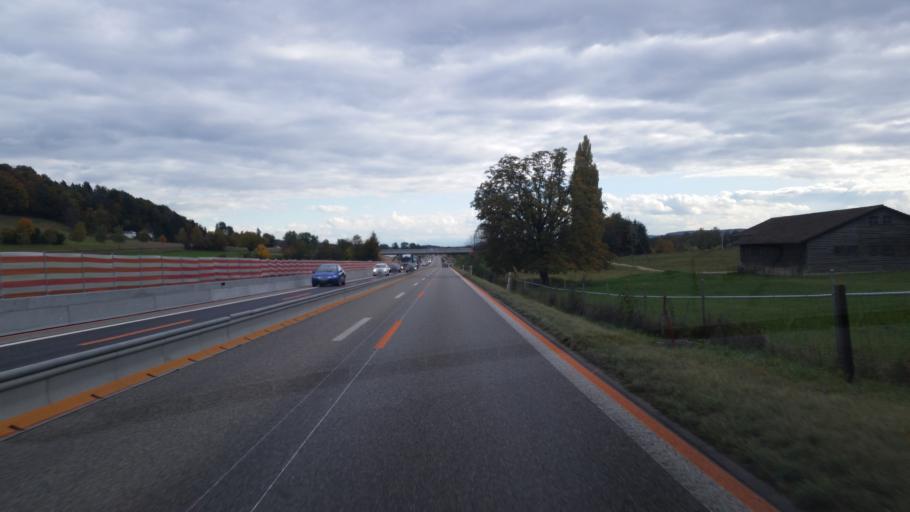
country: CH
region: Zurich
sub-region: Bezirk Buelach
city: Bachenbulach
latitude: 47.4903
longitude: 8.5418
